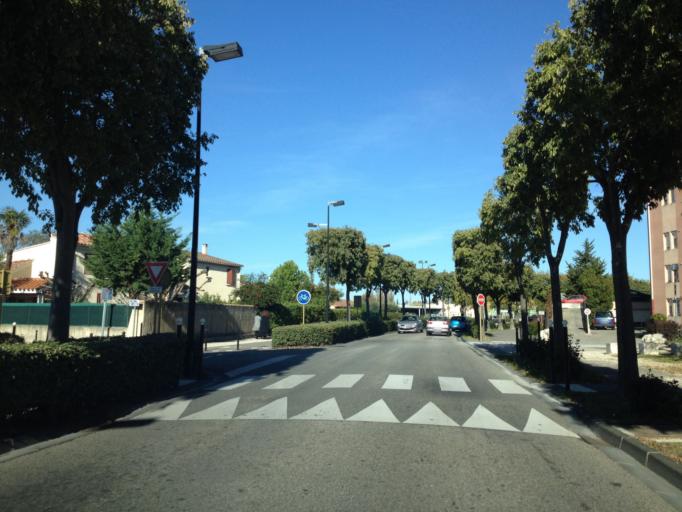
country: FR
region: Provence-Alpes-Cote d'Azur
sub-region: Departement du Vaucluse
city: Orange
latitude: 44.1383
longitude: 4.8004
